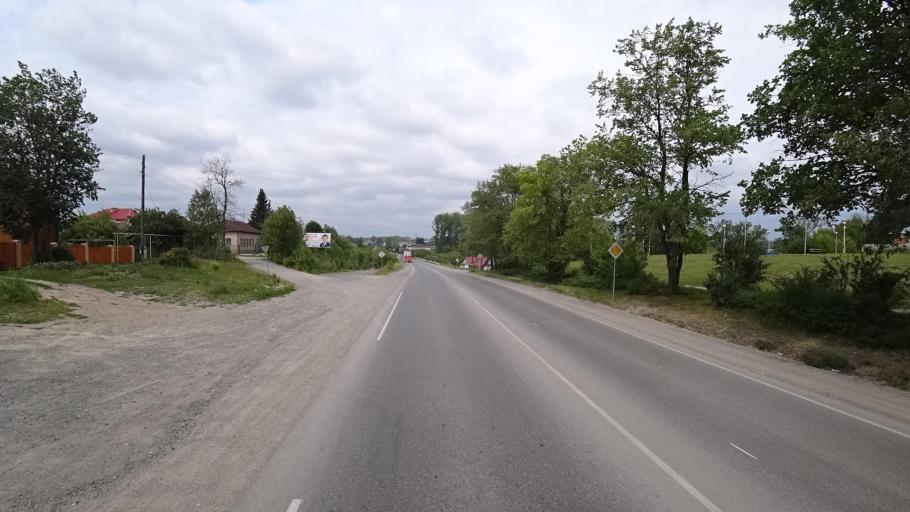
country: RU
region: Sverdlovsk
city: Kamyshlov
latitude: 56.8458
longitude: 62.6886
